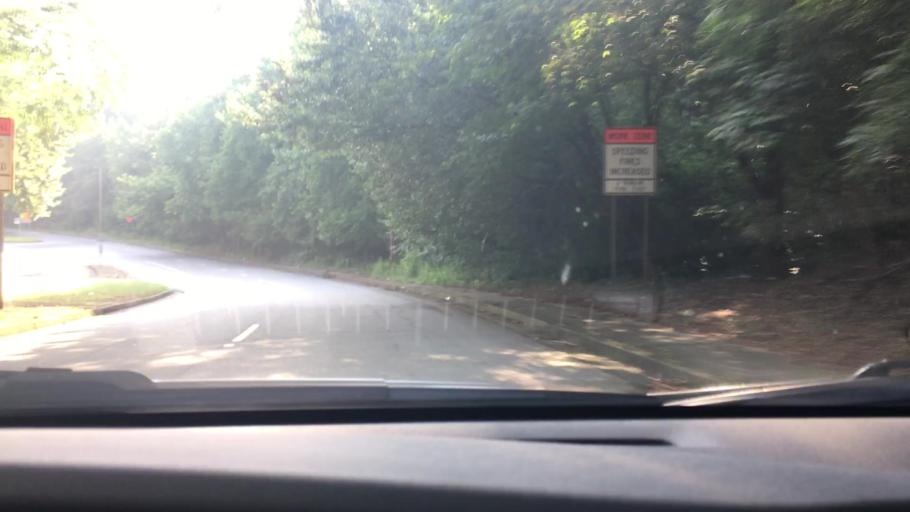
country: US
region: Georgia
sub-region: Cobb County
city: Kennesaw
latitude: 33.9971
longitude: -84.5769
